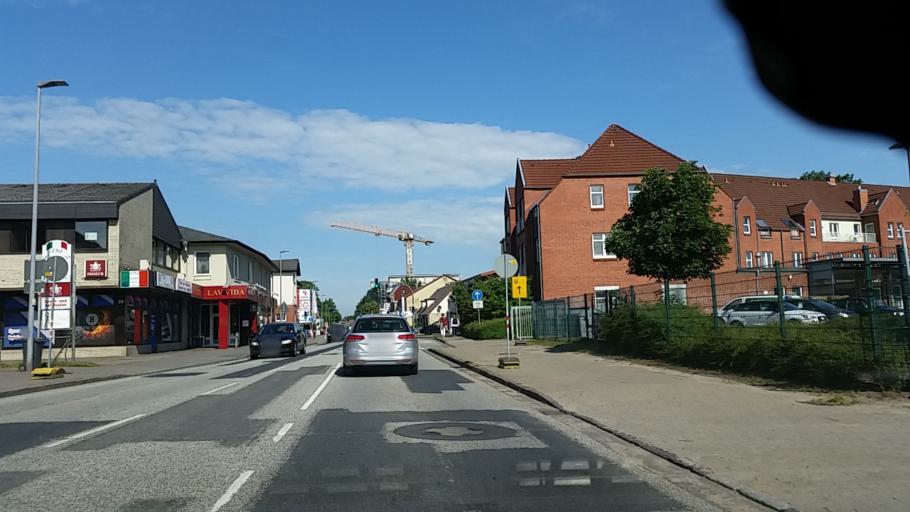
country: DE
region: Schleswig-Holstein
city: Kaltenkirchen
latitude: 53.8355
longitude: 9.9619
